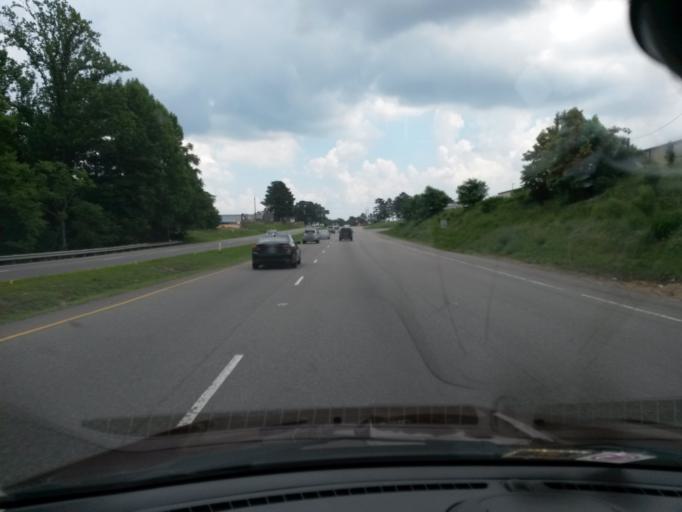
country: US
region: Virginia
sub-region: Chesterfield County
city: Chester
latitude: 37.3519
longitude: -77.3904
